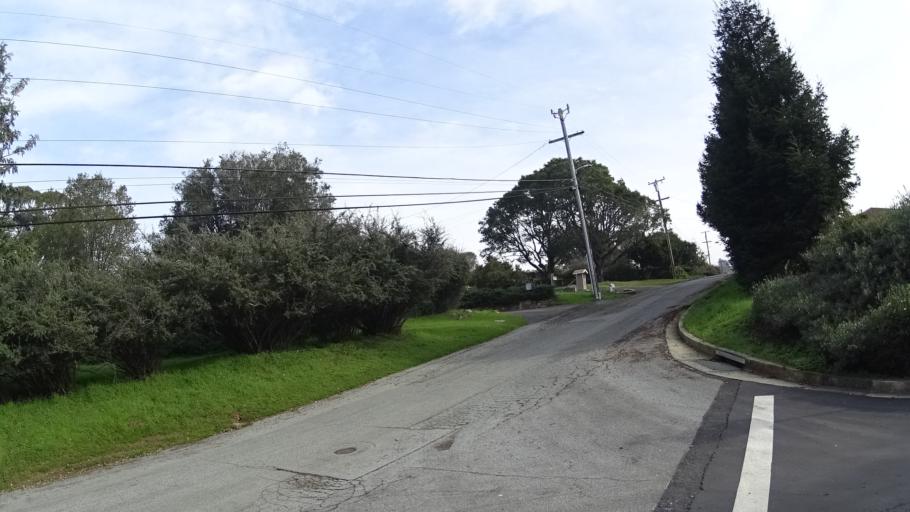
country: US
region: California
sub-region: Alameda County
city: Fairview
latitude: 37.6769
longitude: -122.0551
